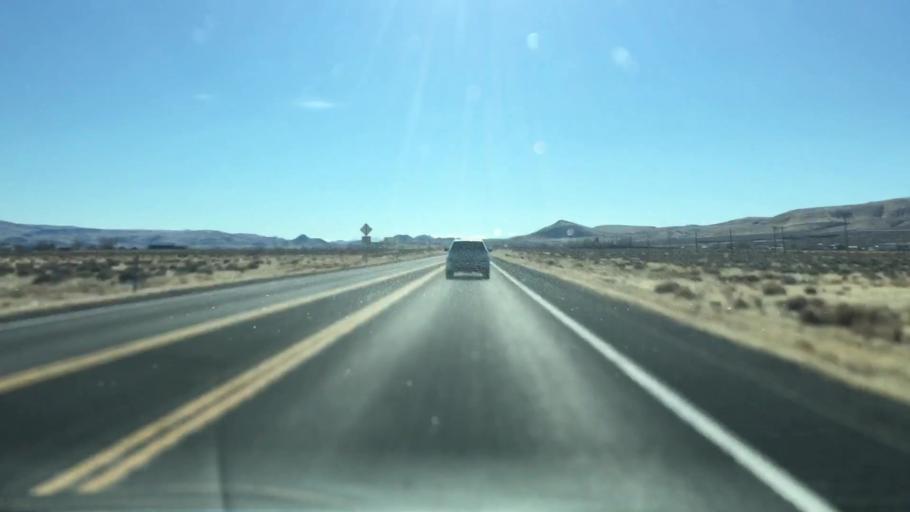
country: US
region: Nevada
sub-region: Lyon County
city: Silver Springs
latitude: 39.3735
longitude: -119.2340
